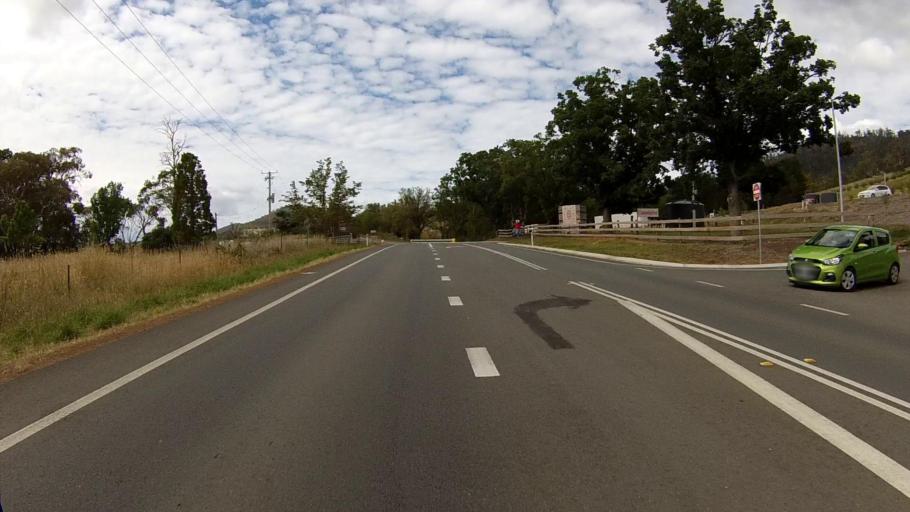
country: AU
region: Tasmania
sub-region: Clarence
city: Cambridge
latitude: -42.8031
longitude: 147.4228
